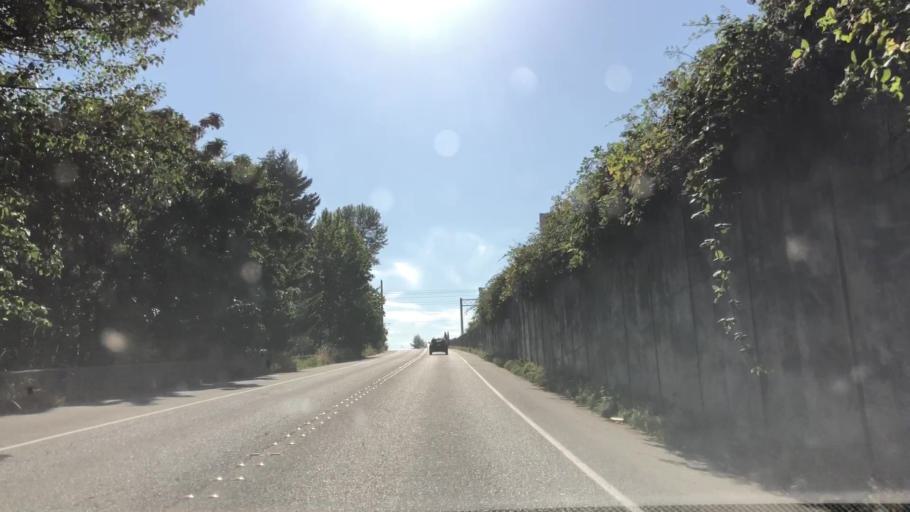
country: US
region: Washington
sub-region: King County
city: Eastgate
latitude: 47.5804
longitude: -122.1609
